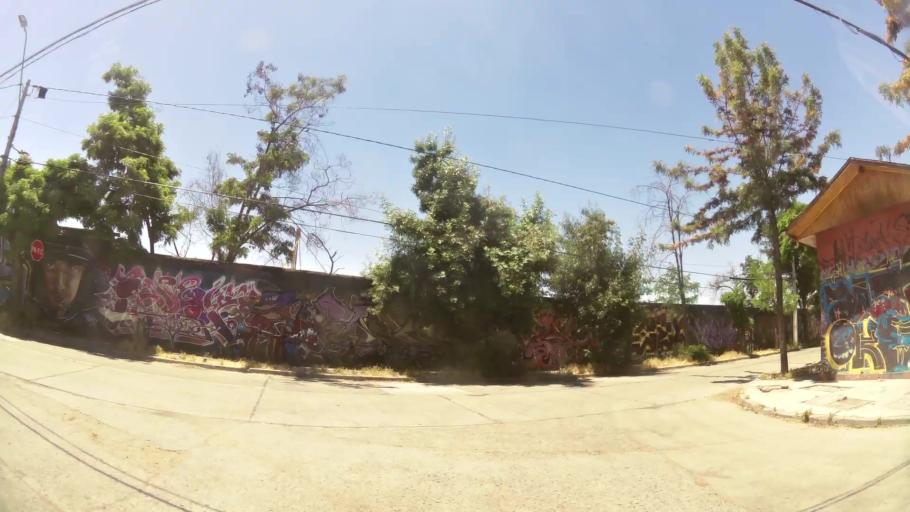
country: CL
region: Santiago Metropolitan
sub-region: Provincia de Maipo
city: San Bernardo
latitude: -33.5986
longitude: -70.6973
